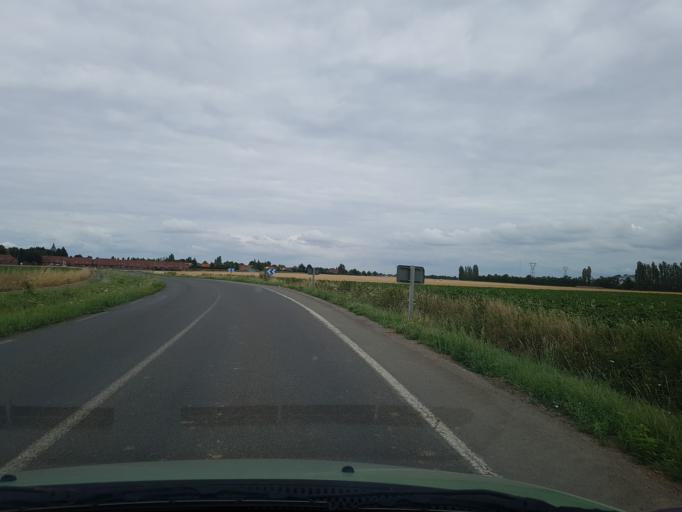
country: FR
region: Nord-Pas-de-Calais
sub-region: Departement du Nord
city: Annoeullin
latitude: 50.5152
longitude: 2.9270
